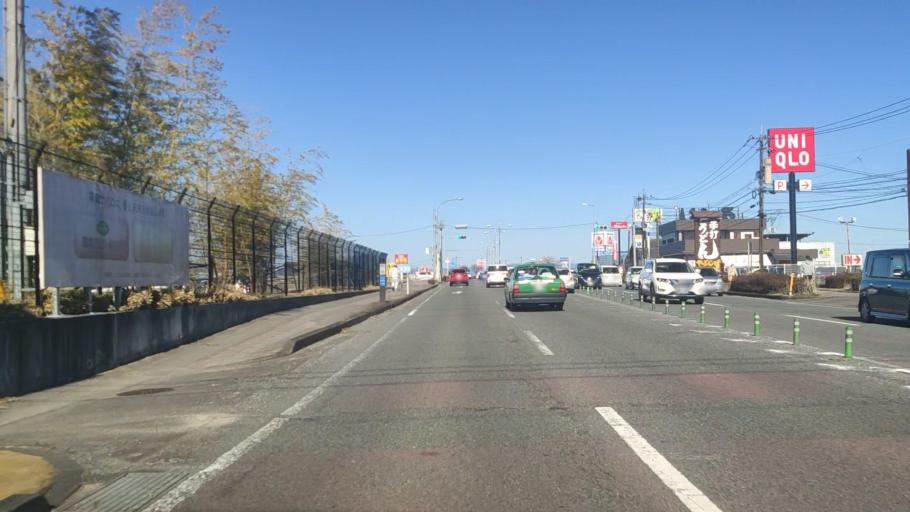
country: JP
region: Miyazaki
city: Miyakonojo
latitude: 31.7479
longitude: 131.0777
